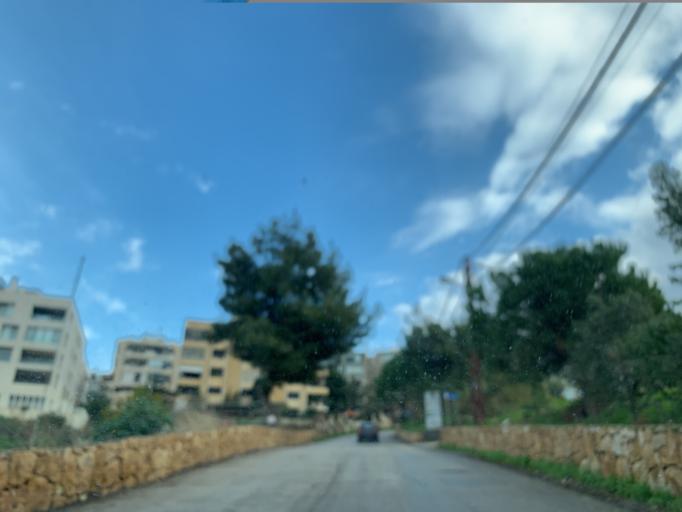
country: LB
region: Mont-Liban
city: Baabda
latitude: 33.8515
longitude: 35.5660
